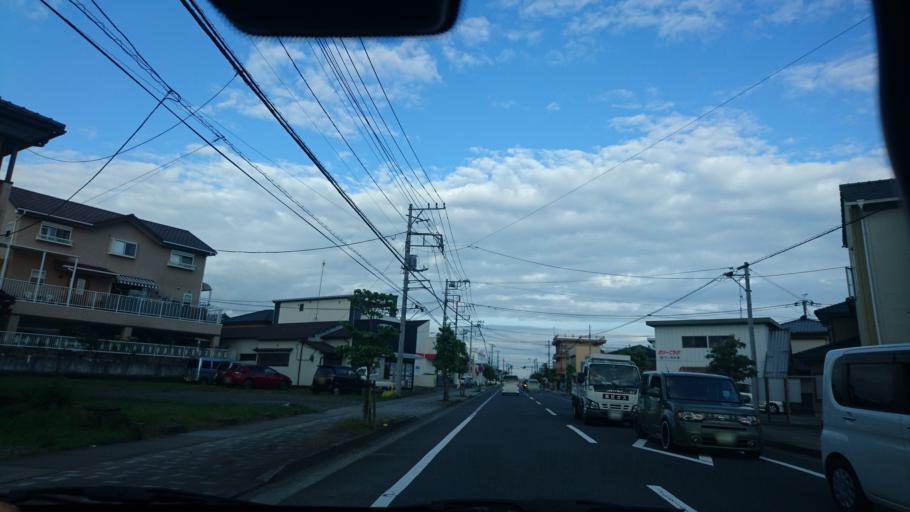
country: JP
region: Shizuoka
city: Fujinomiya
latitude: 35.2342
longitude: 138.6105
